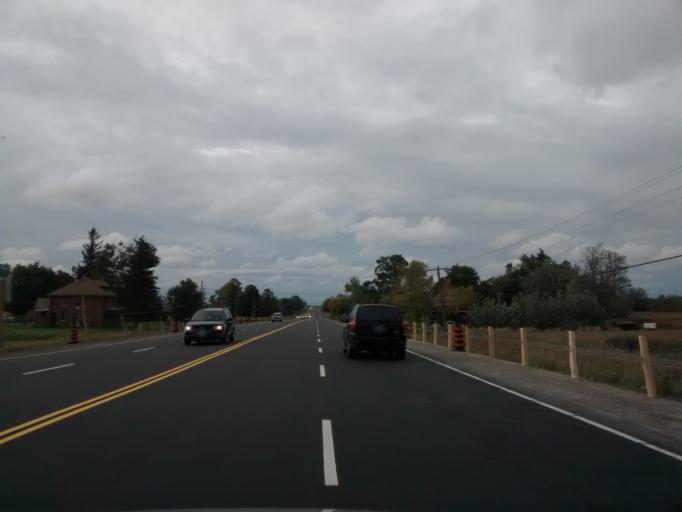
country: CA
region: Ontario
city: Ancaster
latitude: 43.1048
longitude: -79.9379
